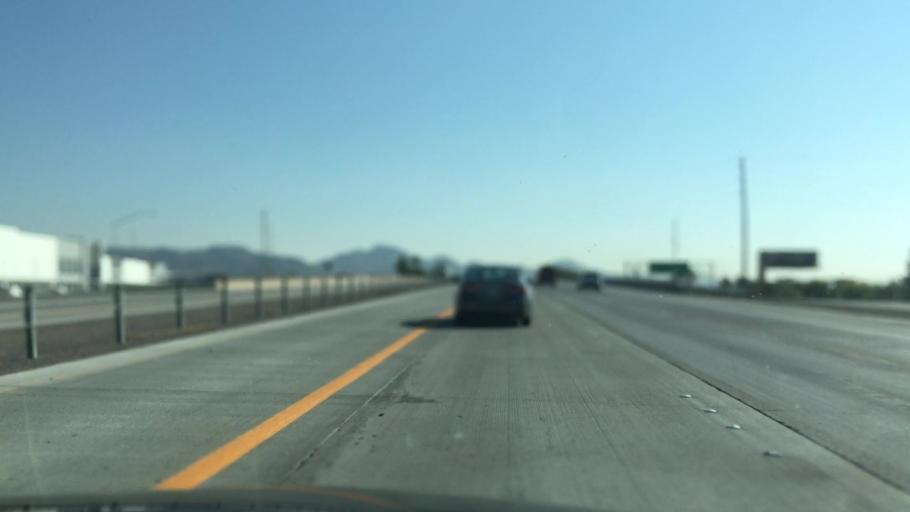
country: US
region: Nevada
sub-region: Clark County
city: Nellis Air Force Base
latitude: 36.2554
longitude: -115.0827
